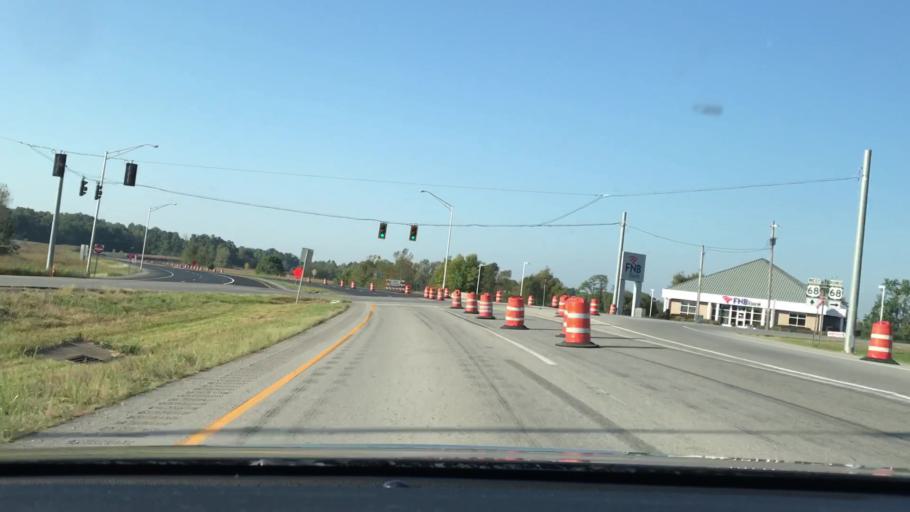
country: US
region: Kentucky
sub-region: Trigg County
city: Cadiz
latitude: 36.8666
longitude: -87.7957
